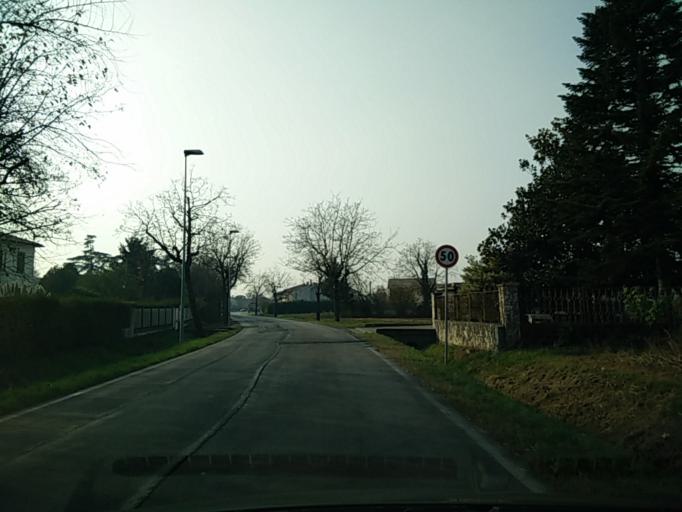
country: IT
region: Veneto
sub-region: Provincia di Treviso
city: Salvatronda
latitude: 45.6757
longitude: 11.9832
